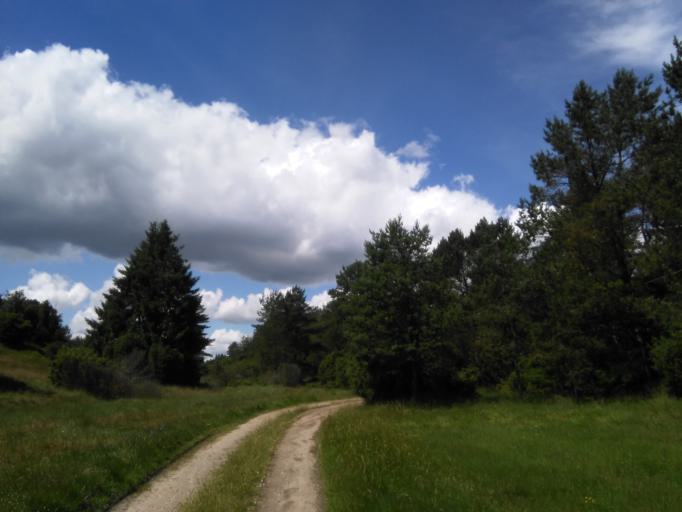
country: DK
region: Central Jutland
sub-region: Silkeborg Kommune
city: Virklund
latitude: 56.0777
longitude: 9.4499
